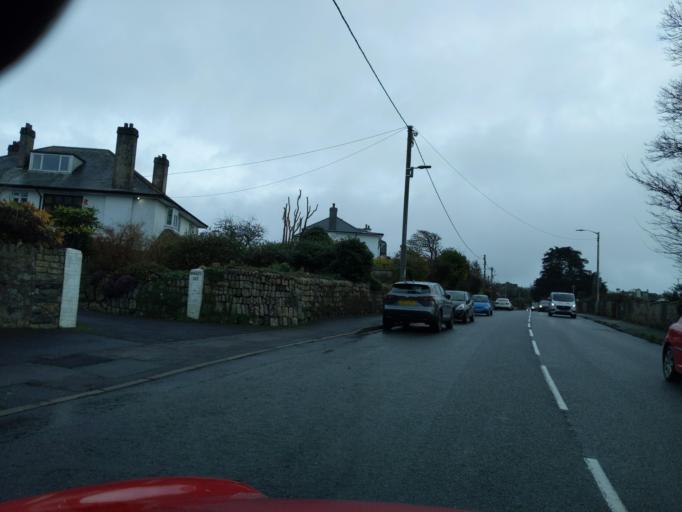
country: GB
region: England
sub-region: Devon
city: Plympton
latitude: 50.3869
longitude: -4.0456
